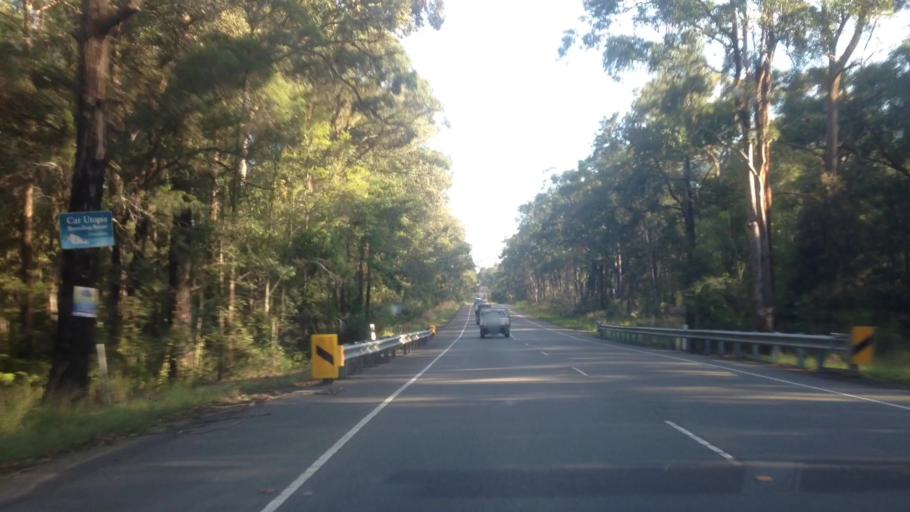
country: AU
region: New South Wales
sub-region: Lake Macquarie Shire
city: Dora Creek
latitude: -33.1354
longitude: 151.4772
